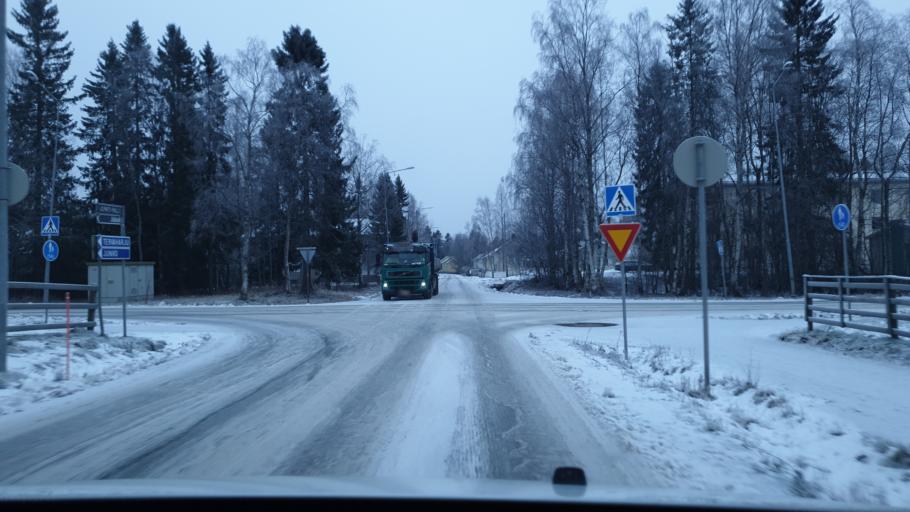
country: FI
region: Lapland
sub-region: Kemi-Tornio
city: Kemi
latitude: 65.7343
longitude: 24.6099
